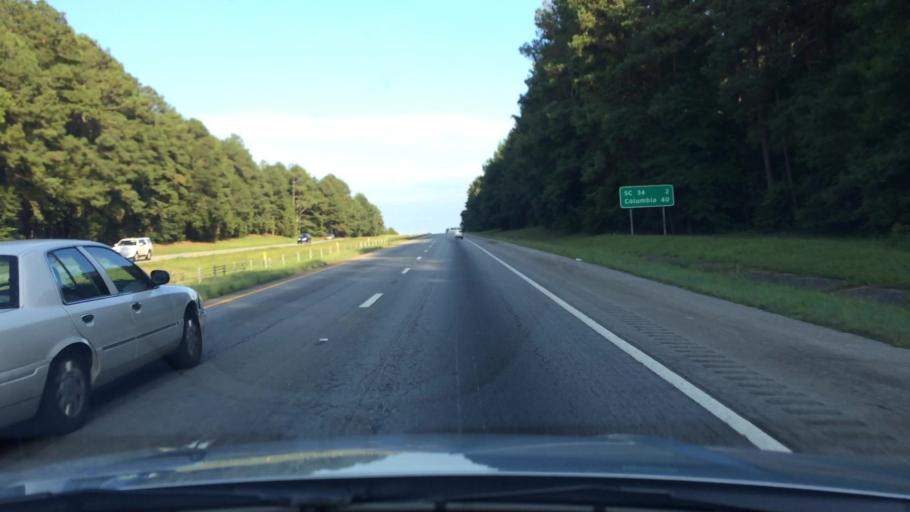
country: US
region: South Carolina
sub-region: Newberry County
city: Newberry
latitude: 34.3253
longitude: -81.5995
